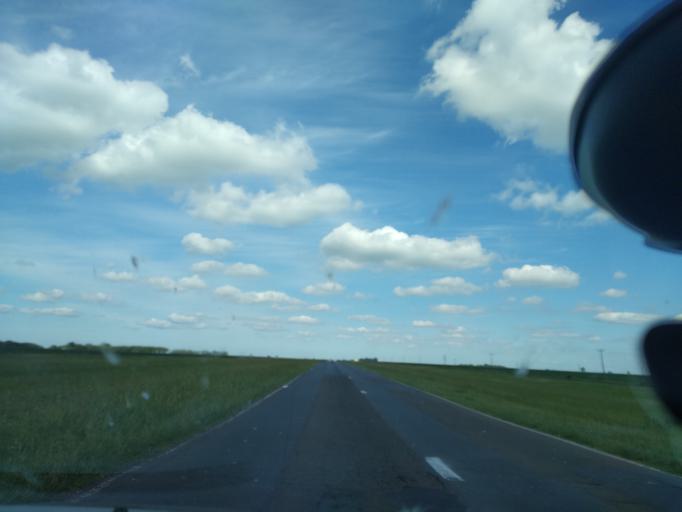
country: AR
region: Santa Fe
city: Carcarana
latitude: -32.8909
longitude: -61.0897
